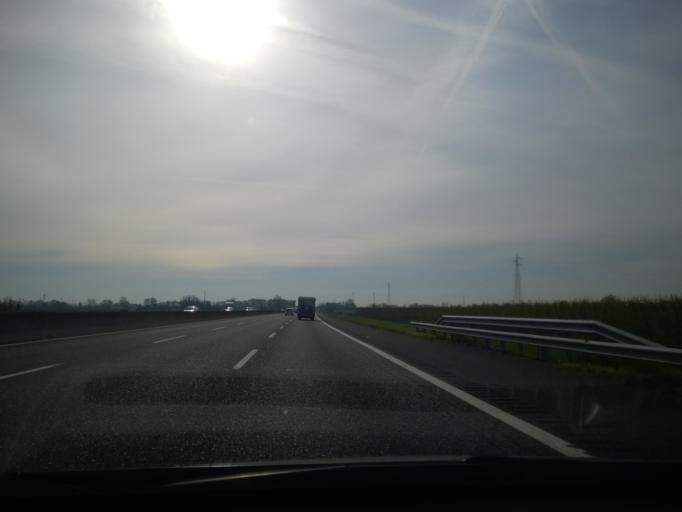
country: IT
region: Emilia-Romagna
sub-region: Provincia di Ravenna
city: Granarolo
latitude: 44.2907
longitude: 11.9885
